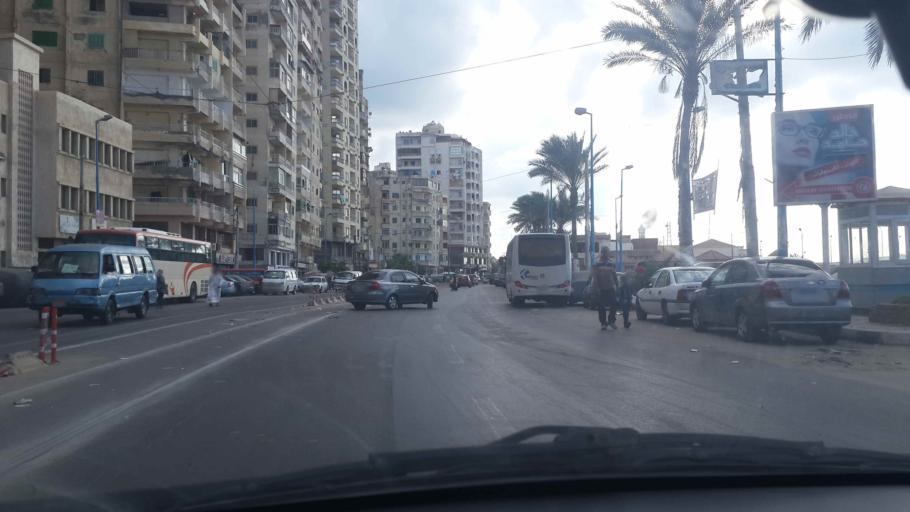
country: EG
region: Alexandria
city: Alexandria
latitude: 31.2049
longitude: 29.8775
